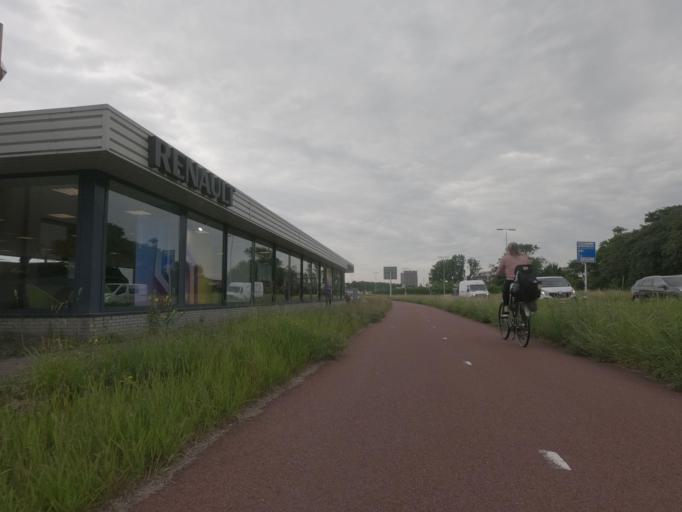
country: NL
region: North Holland
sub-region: Gemeente Zaanstad
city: Zaandam
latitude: 52.4302
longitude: 4.8248
